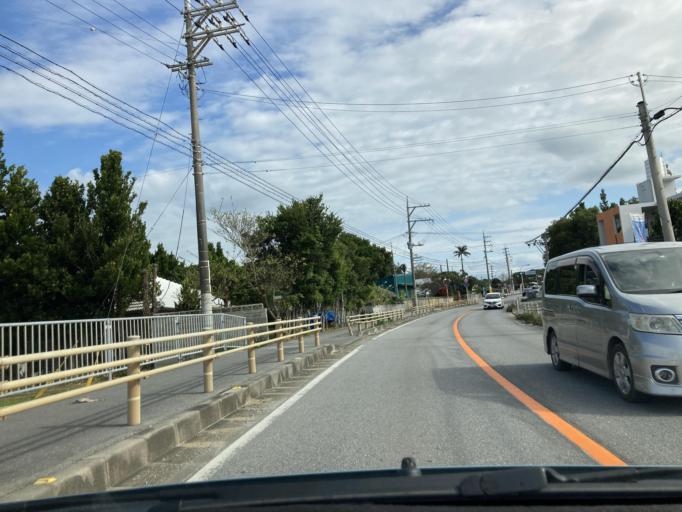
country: JP
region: Okinawa
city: Nago
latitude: 26.6954
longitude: 127.9529
